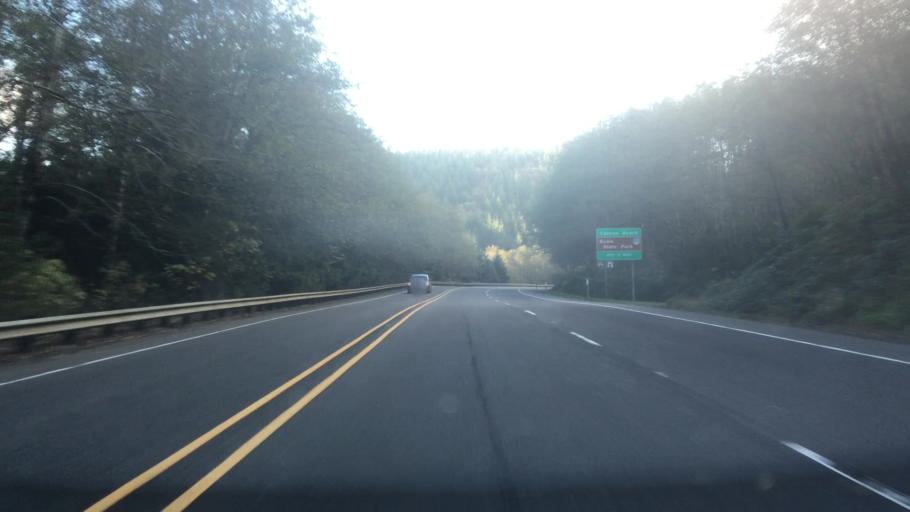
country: US
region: Oregon
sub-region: Clatsop County
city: Cannon Beach
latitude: 45.9177
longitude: -123.9383
